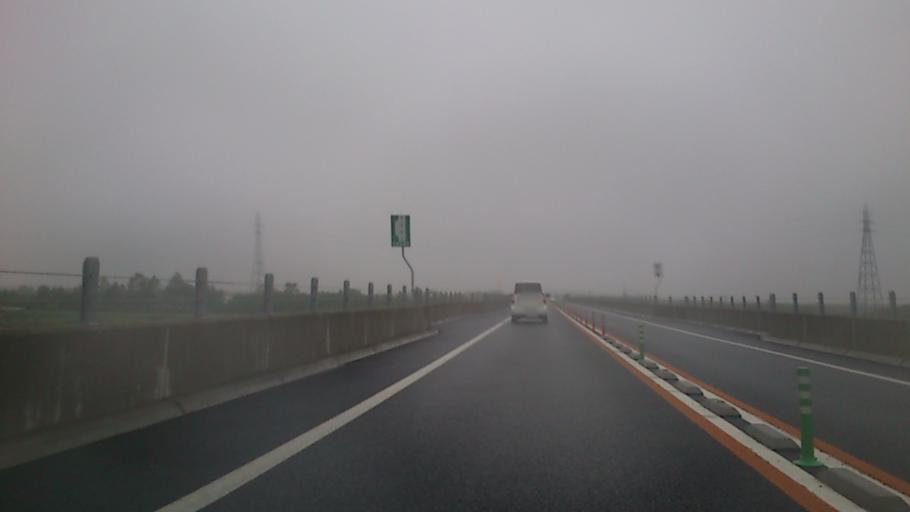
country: JP
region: Hokkaido
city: Kushiro
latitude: 43.0338
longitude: 144.3828
